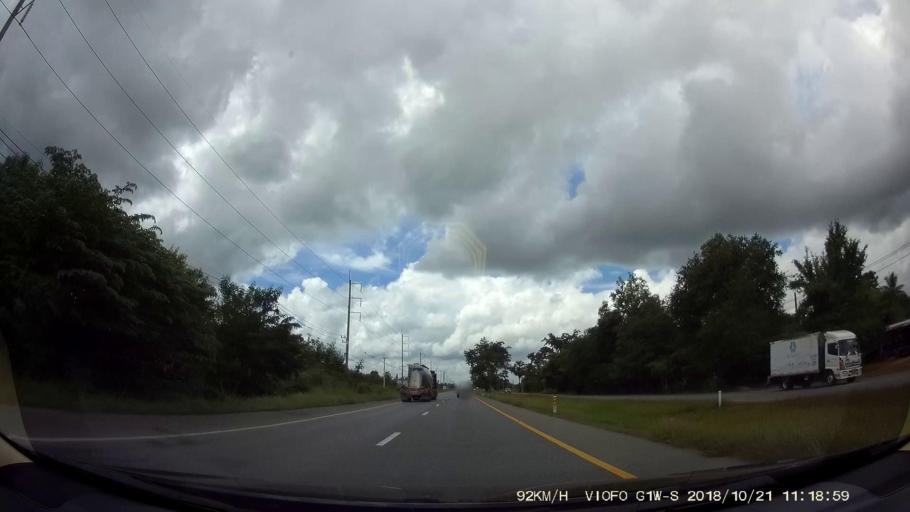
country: TH
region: Chaiyaphum
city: Chaiyaphum
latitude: 15.8728
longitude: 102.0909
